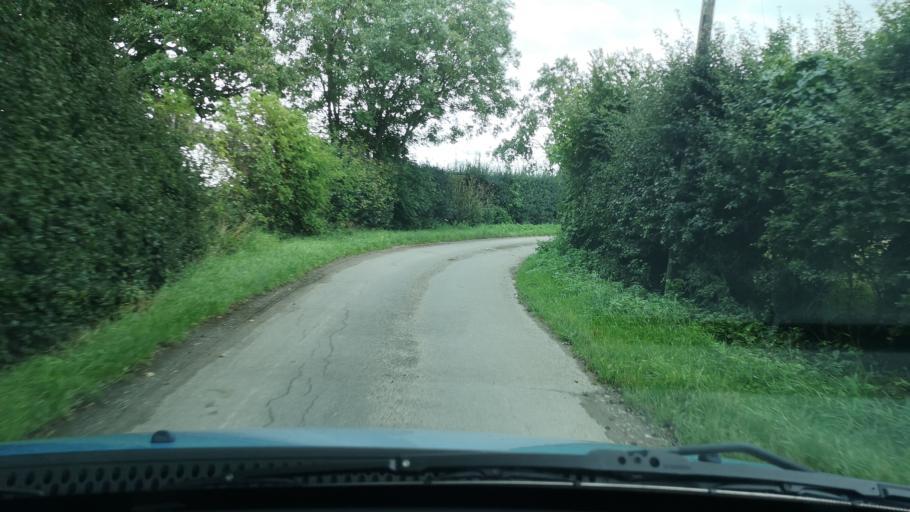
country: GB
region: England
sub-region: City and Borough of Wakefield
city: Featherstone
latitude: 53.6568
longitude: -1.3557
